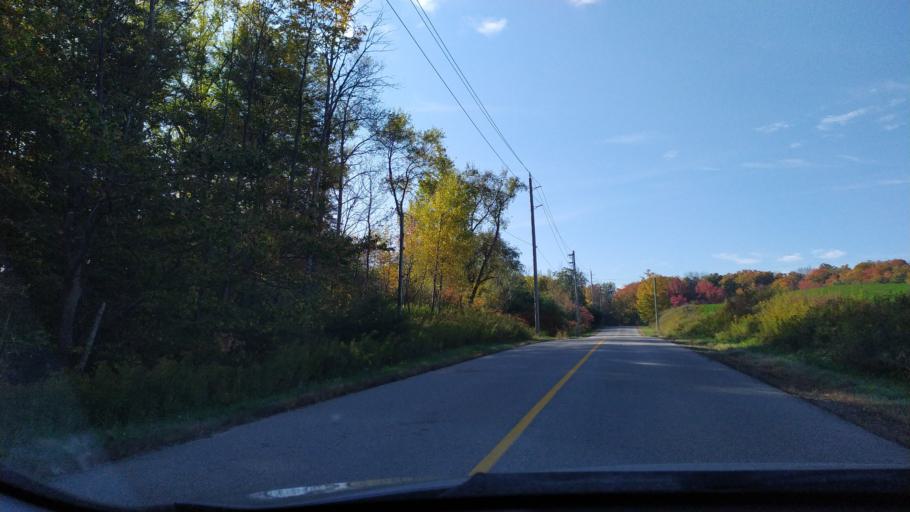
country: CA
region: Ontario
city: Waterloo
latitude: 43.4888
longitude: -80.6577
